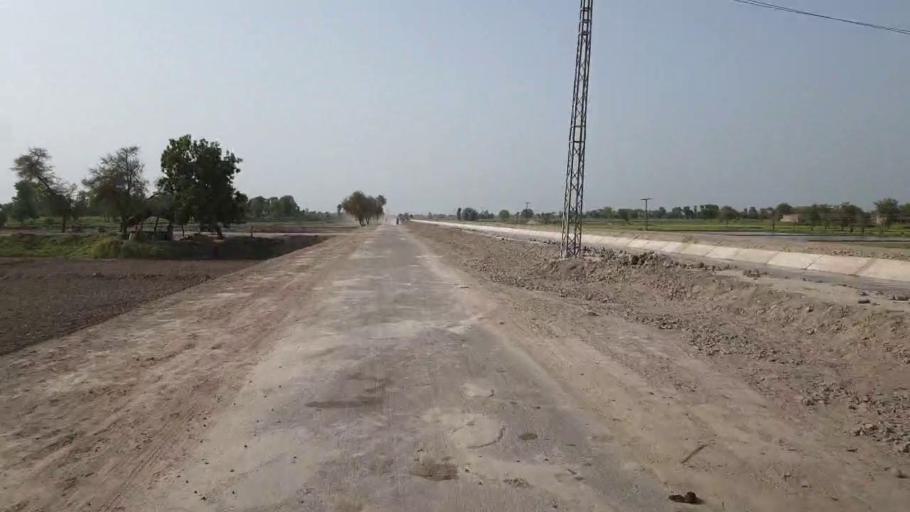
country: PK
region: Sindh
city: Daur
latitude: 26.3325
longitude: 68.1644
